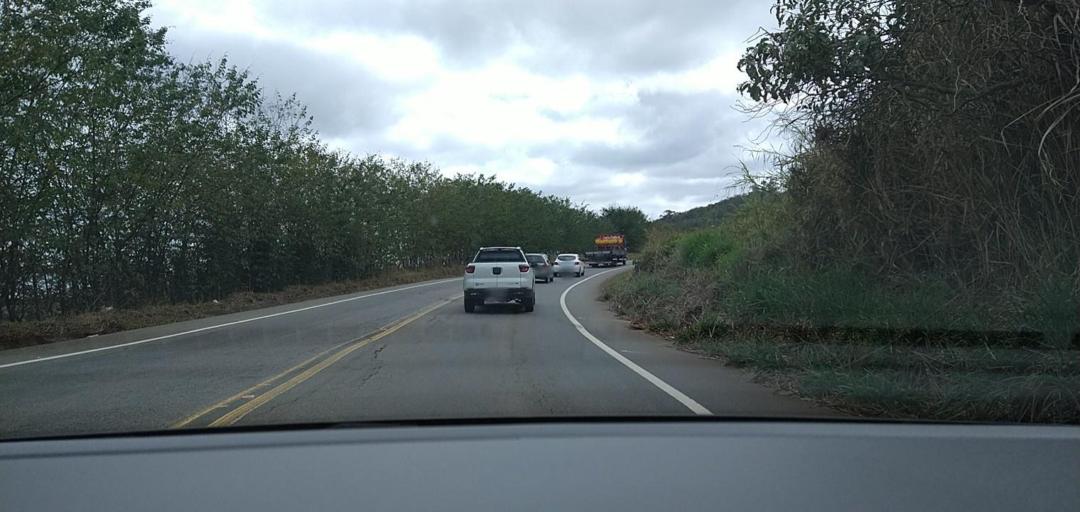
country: BR
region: Minas Gerais
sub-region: Ponte Nova
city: Ponte Nova
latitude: -20.5350
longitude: -42.8924
